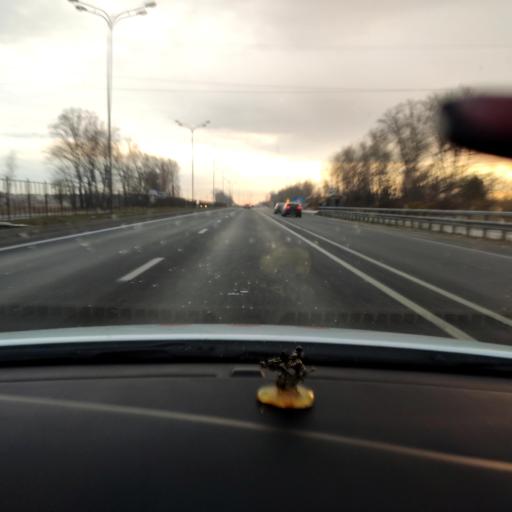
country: RU
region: Tatarstan
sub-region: Zelenodol'skiy Rayon
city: Vasil'yevo
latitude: 55.8711
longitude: 48.6692
